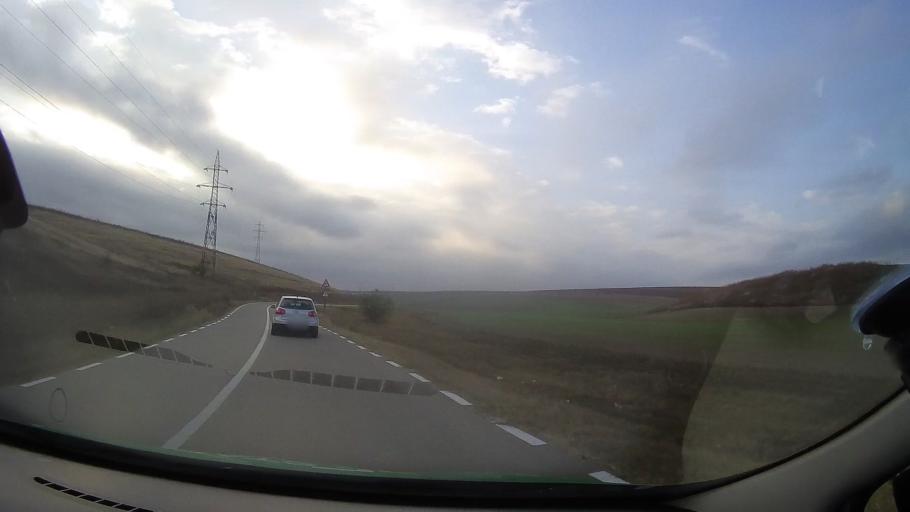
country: RO
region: Constanta
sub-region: Comuna Pestera
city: Pestera
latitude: 44.2035
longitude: 28.1500
